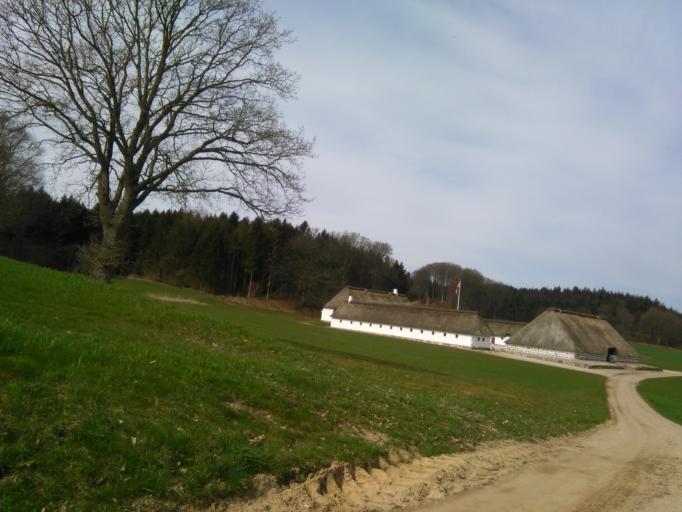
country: DK
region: Central Jutland
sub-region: Odder Kommune
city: Odder
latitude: 55.8890
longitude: 10.1028
